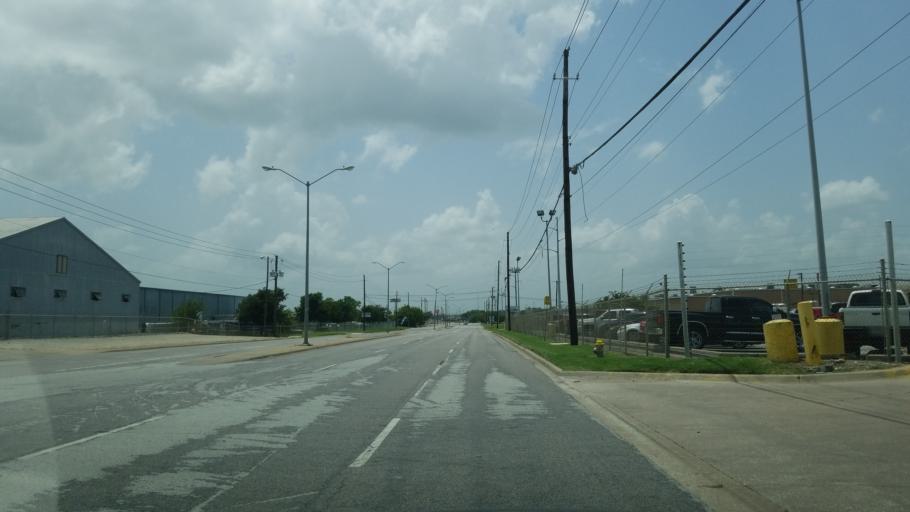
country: US
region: Texas
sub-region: Dallas County
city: Cockrell Hill
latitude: 32.7790
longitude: -96.8847
